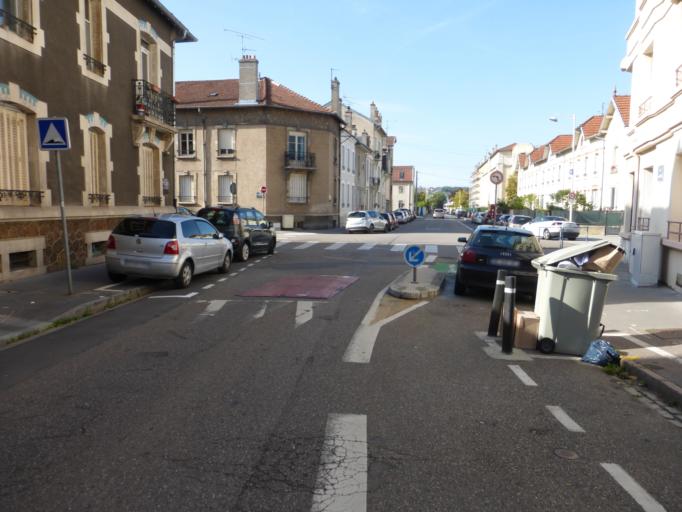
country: FR
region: Lorraine
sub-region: Departement de Meurthe-et-Moselle
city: Nancy
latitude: 48.6748
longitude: 6.1723
